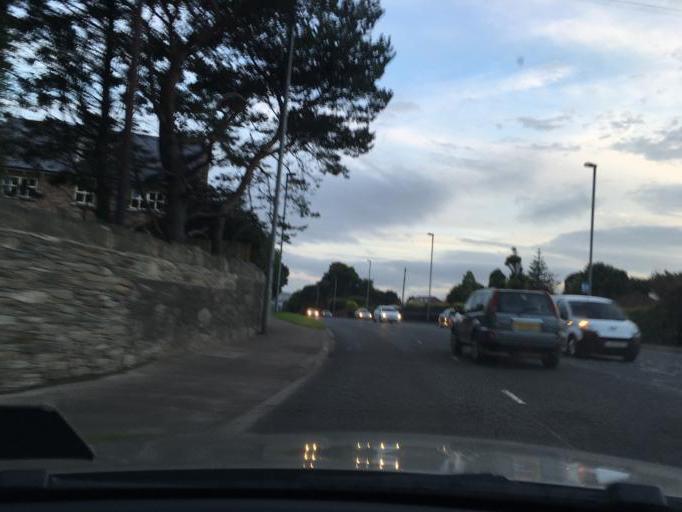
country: GB
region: Northern Ireland
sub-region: City of Derry
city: Derry
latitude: 55.0213
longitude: -7.3083
